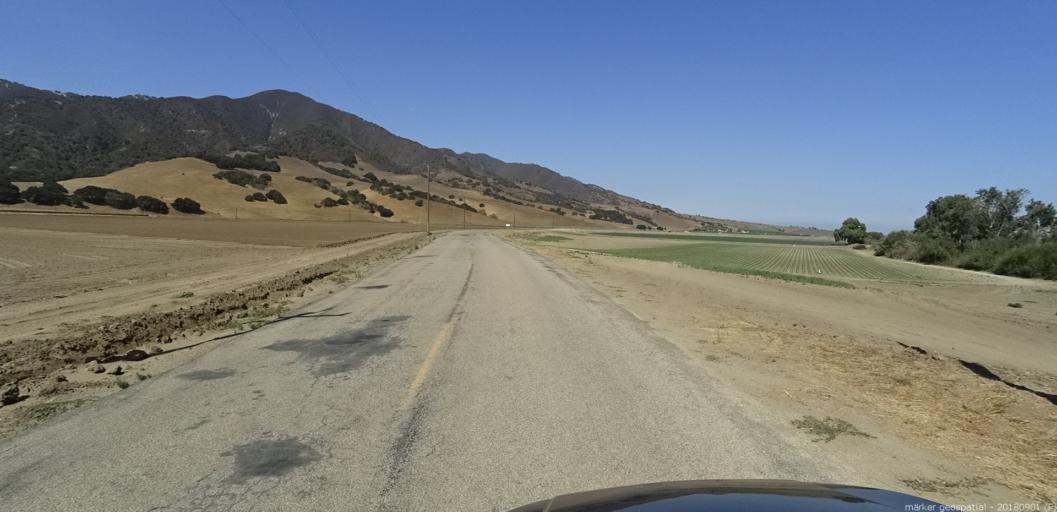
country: US
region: California
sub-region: Monterey County
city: Chualar
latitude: 36.5328
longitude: -121.5356
